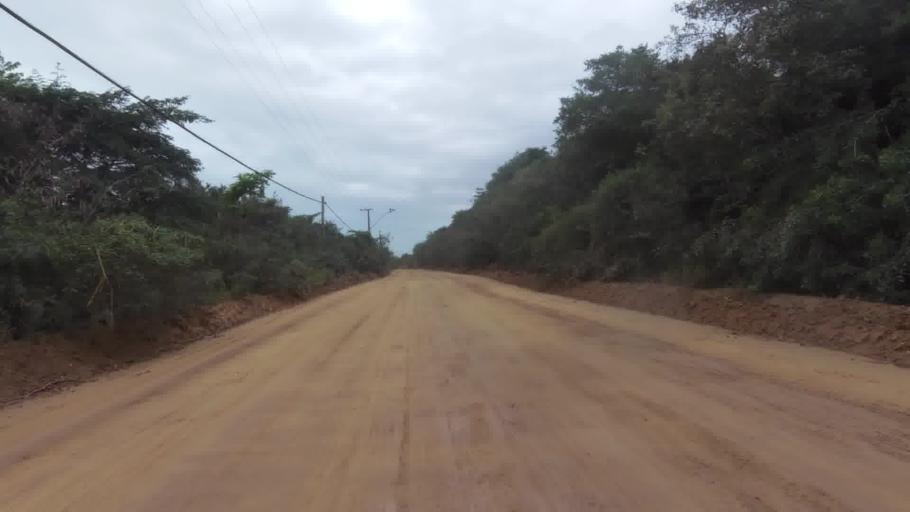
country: BR
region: Espirito Santo
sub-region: Marataizes
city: Marataizes
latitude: -21.0592
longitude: -40.8363
